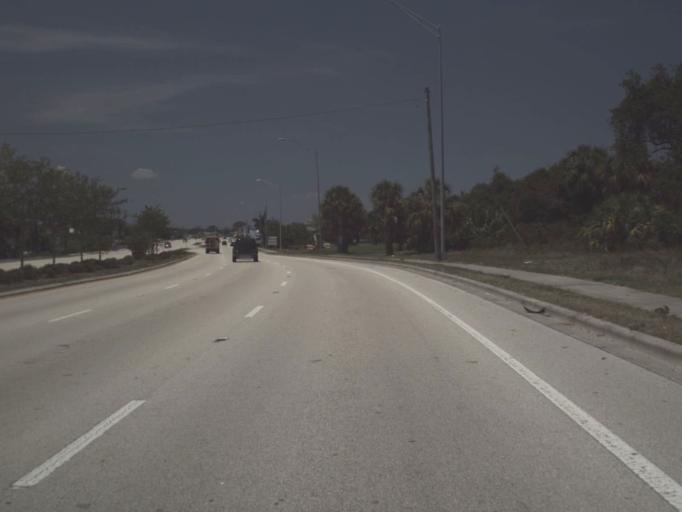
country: US
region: Florida
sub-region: Brevard County
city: Palm Bay
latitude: 28.0576
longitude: -80.5902
